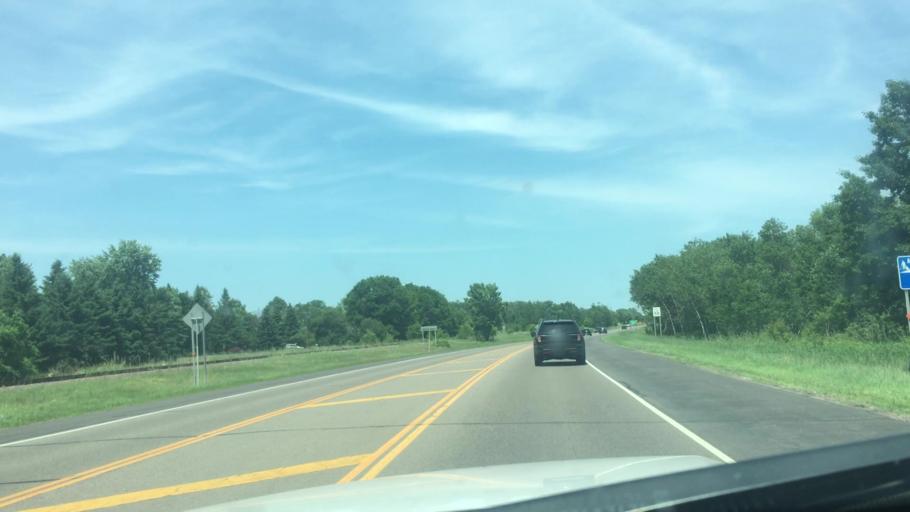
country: US
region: Minnesota
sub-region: Washington County
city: Hugo
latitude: 45.1259
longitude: -93.0030
